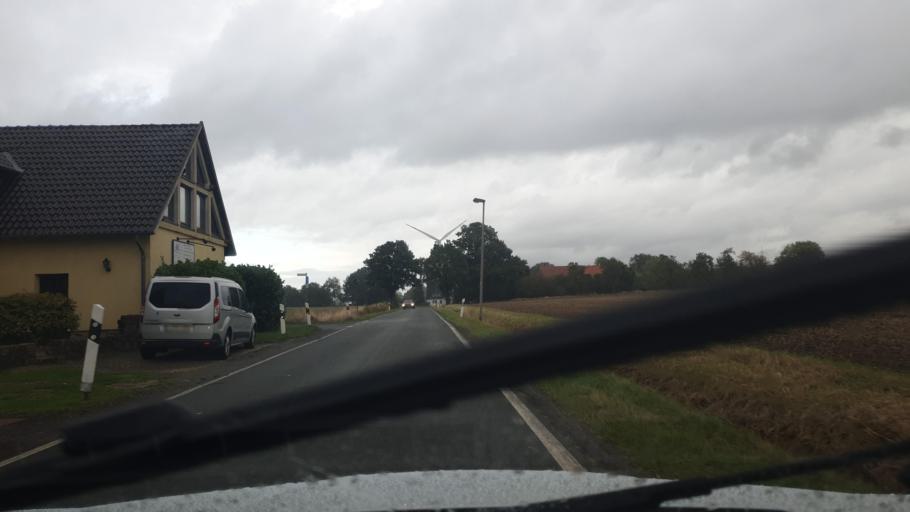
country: DE
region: North Rhine-Westphalia
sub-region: Regierungsbezirk Detmold
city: Vlotho
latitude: 52.2005
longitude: 8.8791
